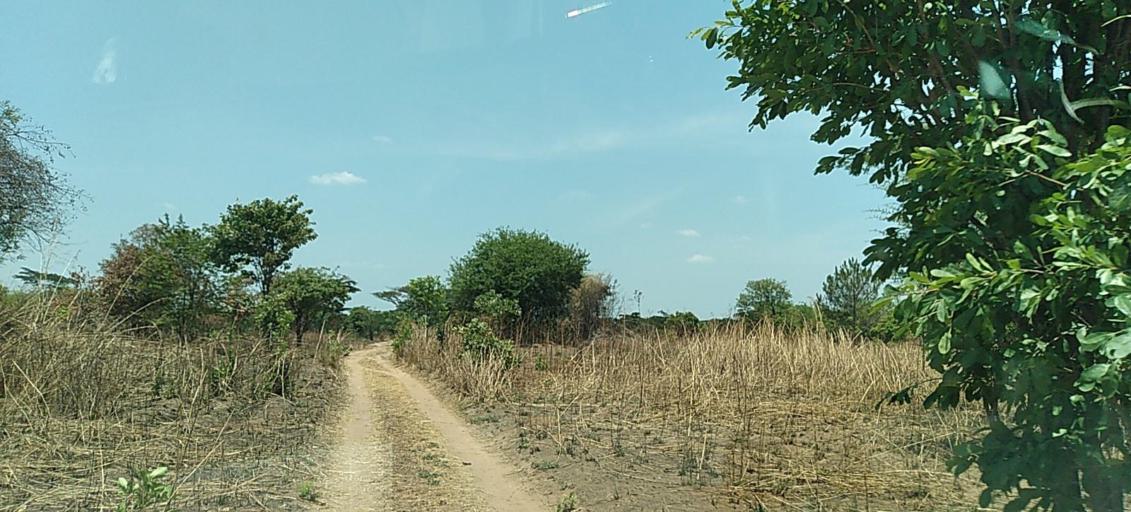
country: ZM
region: Copperbelt
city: Luanshya
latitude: -13.0638
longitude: 28.4068
